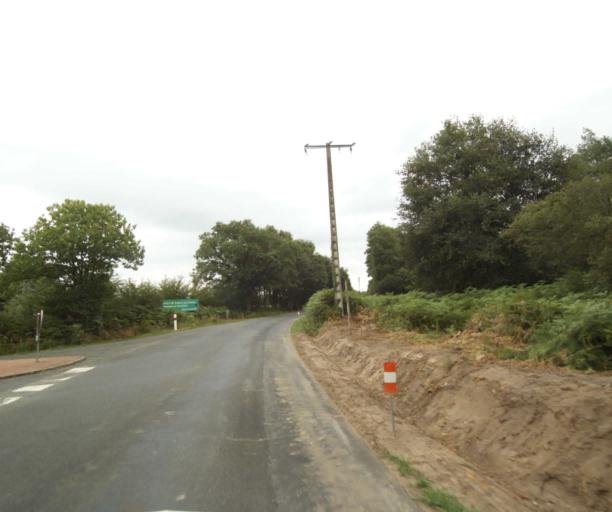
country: FR
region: Pays de la Loire
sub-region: Departement de la Sarthe
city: Sable-sur-Sarthe
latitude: 47.8124
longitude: -0.3568
